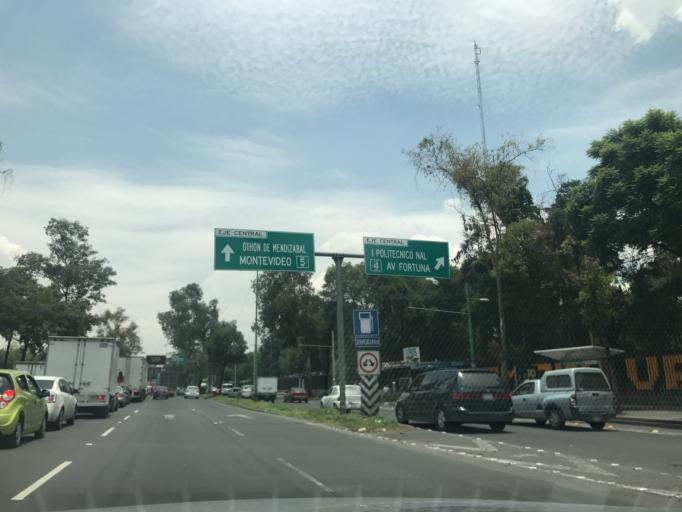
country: MX
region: Mexico
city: Colonia Lindavista
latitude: 19.4837
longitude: -99.1422
